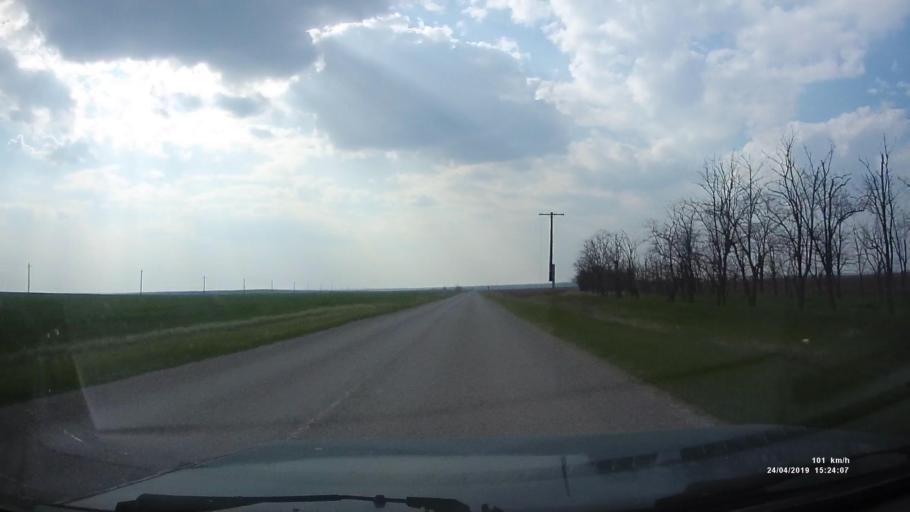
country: RU
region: Rostov
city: Remontnoye
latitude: 46.5463
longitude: 43.0757
